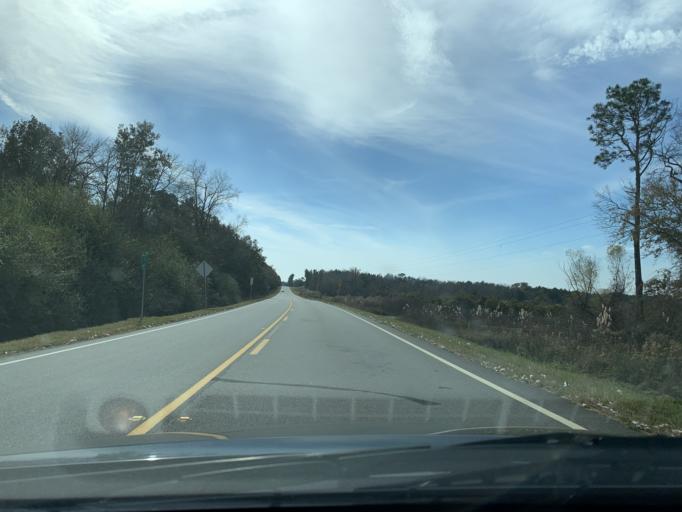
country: US
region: Georgia
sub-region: Turner County
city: Ashburn
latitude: 31.7429
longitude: -83.5695
